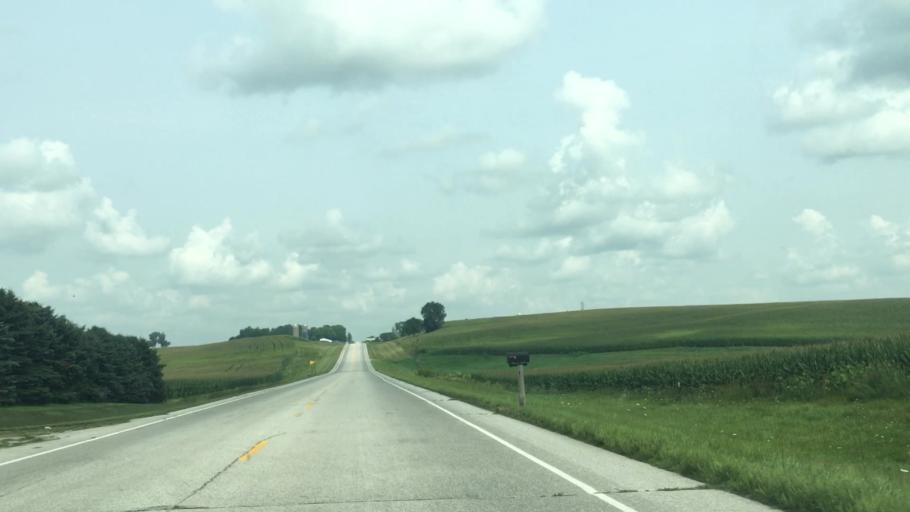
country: US
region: Minnesota
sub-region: Fillmore County
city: Harmony
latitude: 43.6048
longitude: -91.9297
